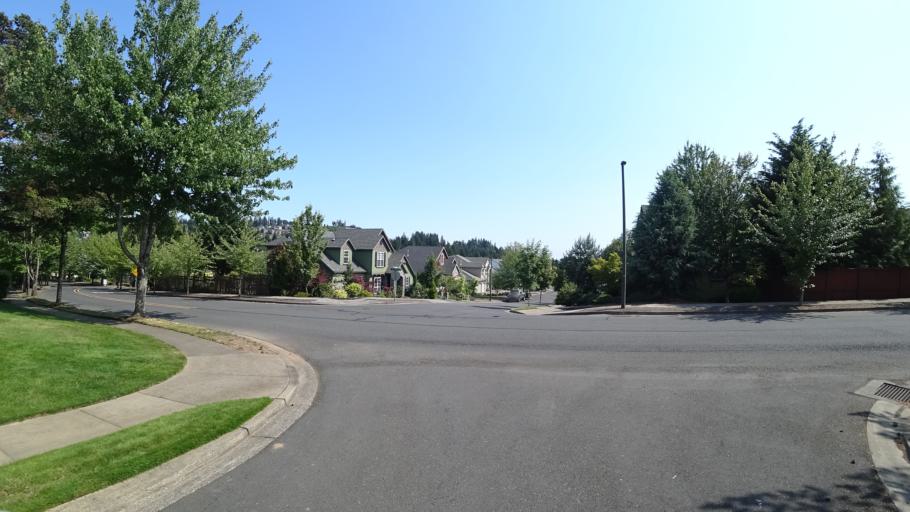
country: US
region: Oregon
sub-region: Clackamas County
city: Happy Valley
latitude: 45.4449
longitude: -122.5348
